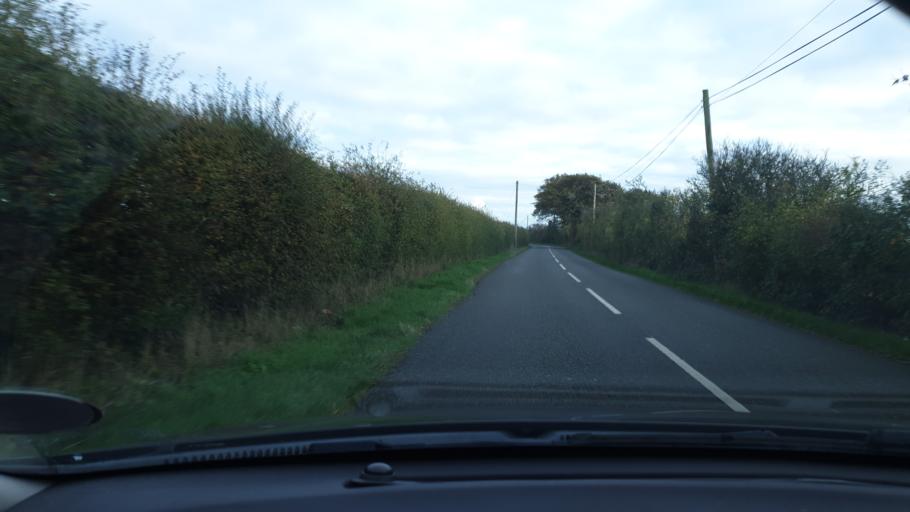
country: GB
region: England
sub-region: Essex
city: Mistley
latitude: 51.9275
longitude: 1.1173
